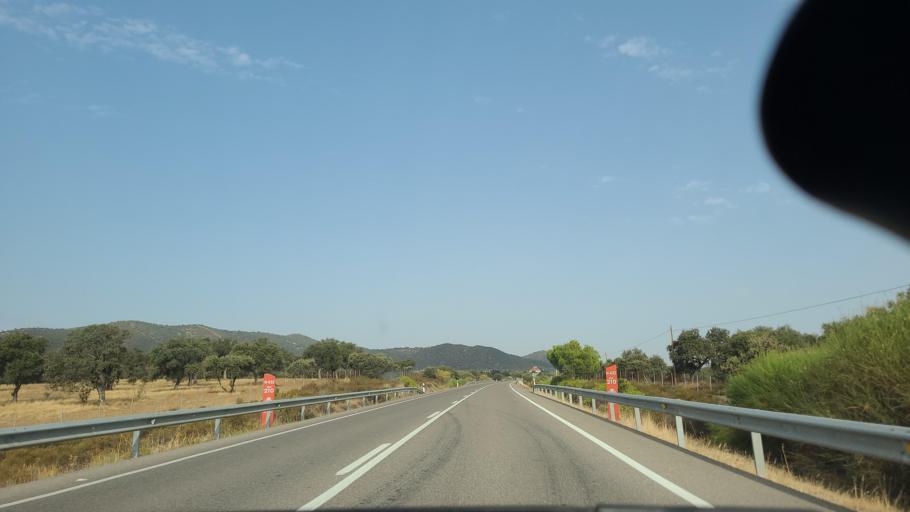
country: ES
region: Andalusia
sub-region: Province of Cordoba
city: Belmez
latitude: 38.2074
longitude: -5.1278
